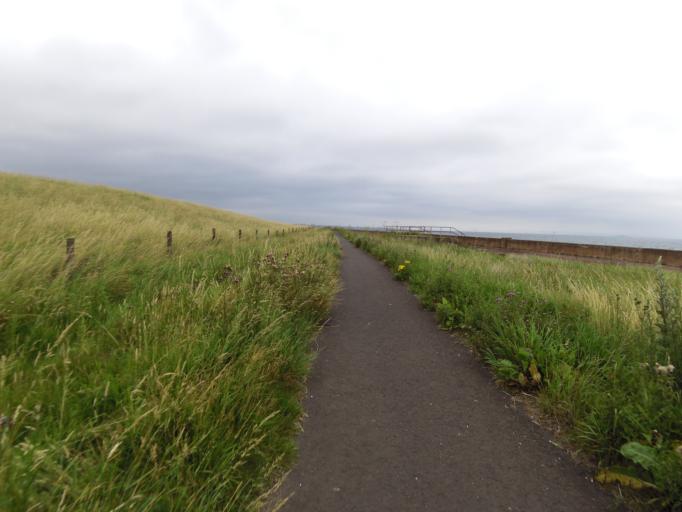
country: GB
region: Scotland
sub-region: East Lothian
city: Musselburgh
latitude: 55.9540
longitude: -3.0352
